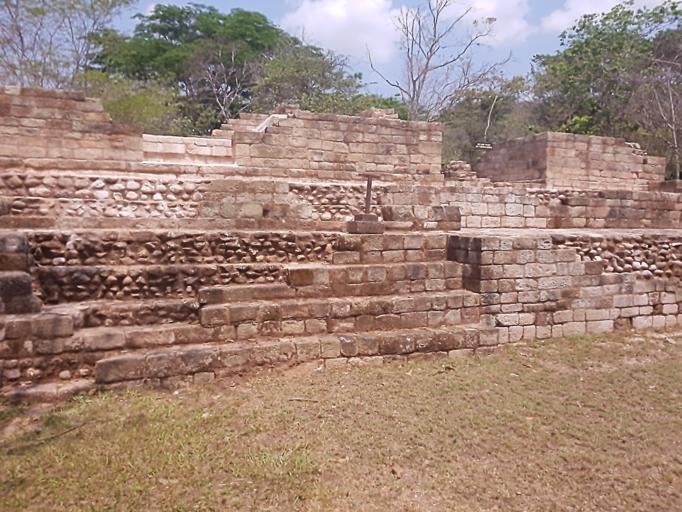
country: HN
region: Copan
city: Copan
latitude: 14.8415
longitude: -89.1421
